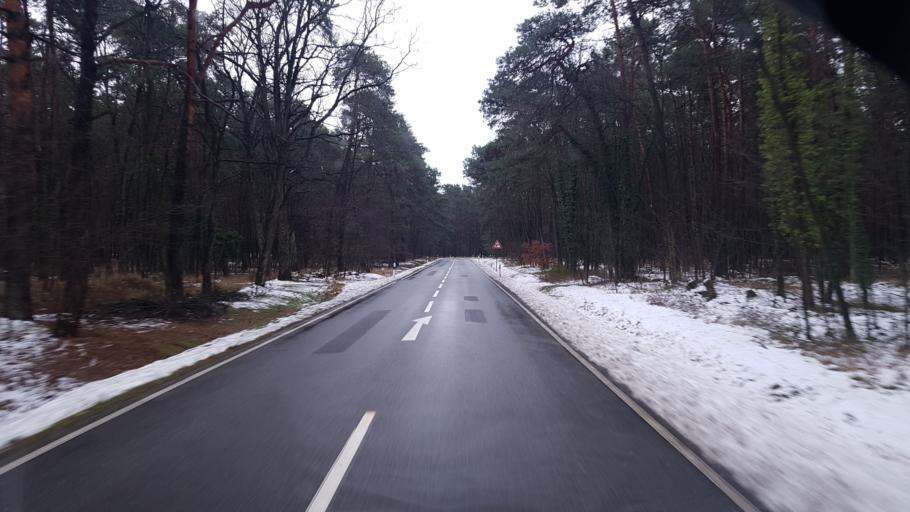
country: DE
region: Brandenburg
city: Schenkendobern
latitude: 51.9045
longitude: 14.6336
